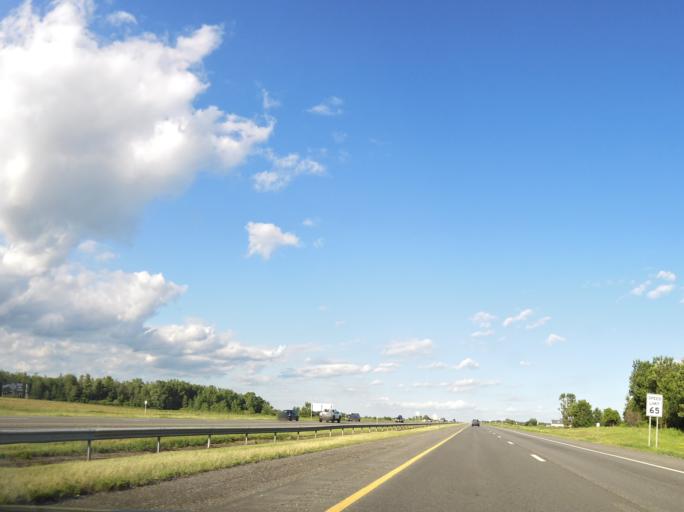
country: US
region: New York
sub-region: Genesee County
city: Batavia
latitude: 43.0196
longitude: -78.1725
